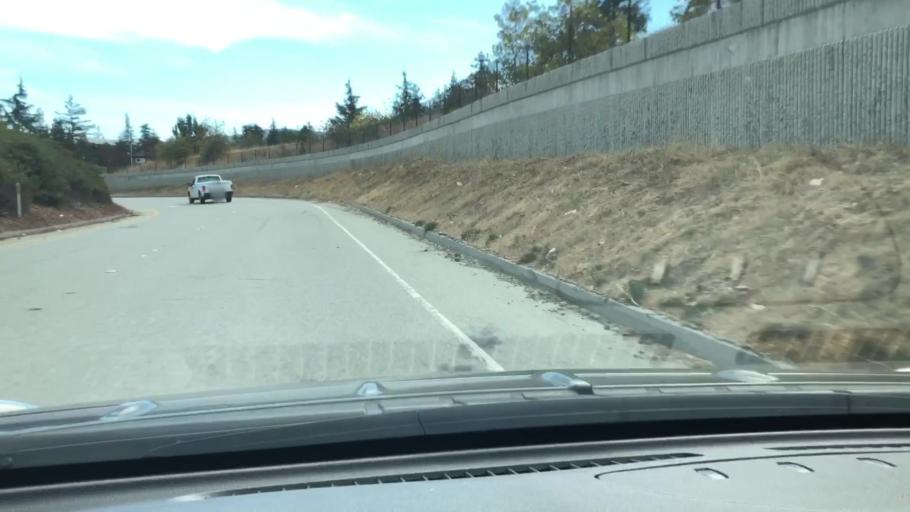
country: US
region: California
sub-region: Santa Clara County
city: Los Gatos
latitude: 37.2582
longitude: -121.9663
